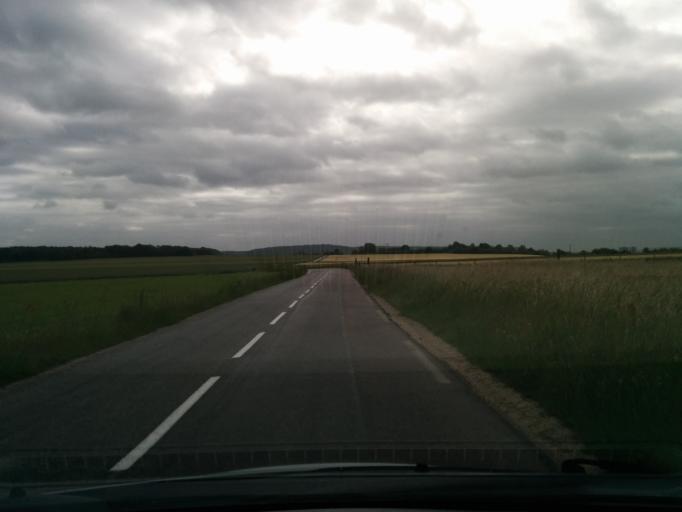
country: FR
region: Ile-de-France
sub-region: Departement des Yvelines
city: Rosny-sur-Seine
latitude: 49.0125
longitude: 1.6541
